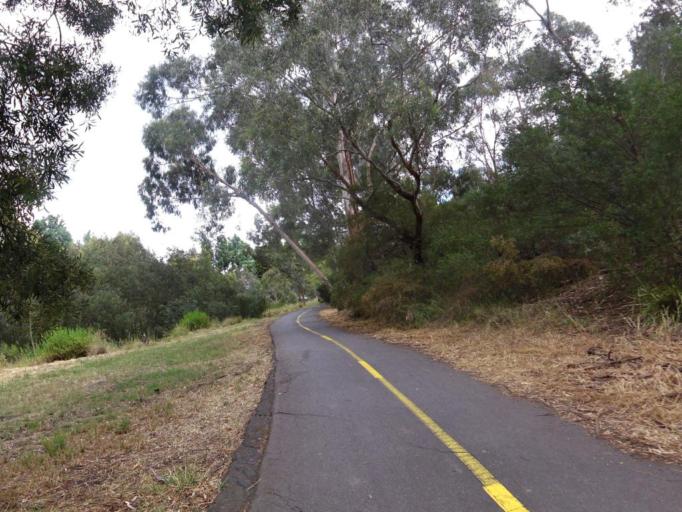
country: AU
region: Victoria
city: Heidelberg West
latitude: -37.7553
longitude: 145.0314
